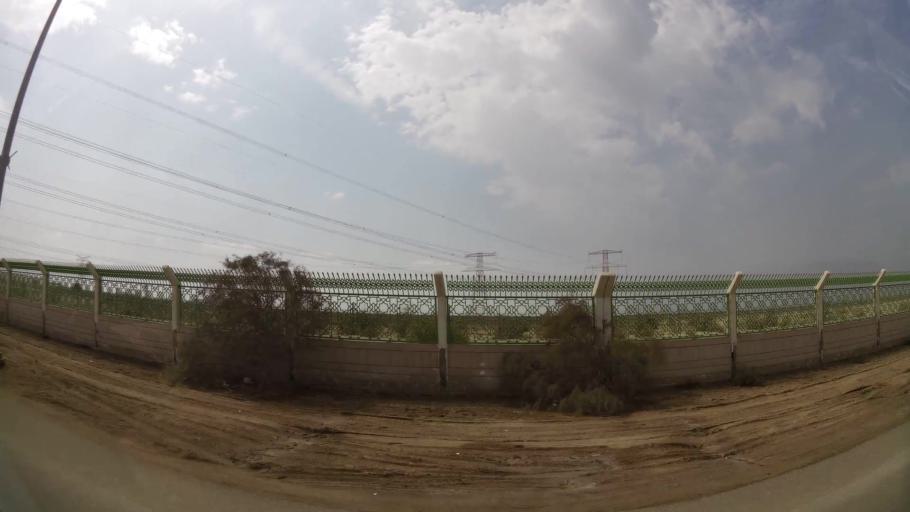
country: AE
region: Abu Dhabi
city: Abu Dhabi
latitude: 24.5255
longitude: 54.6450
